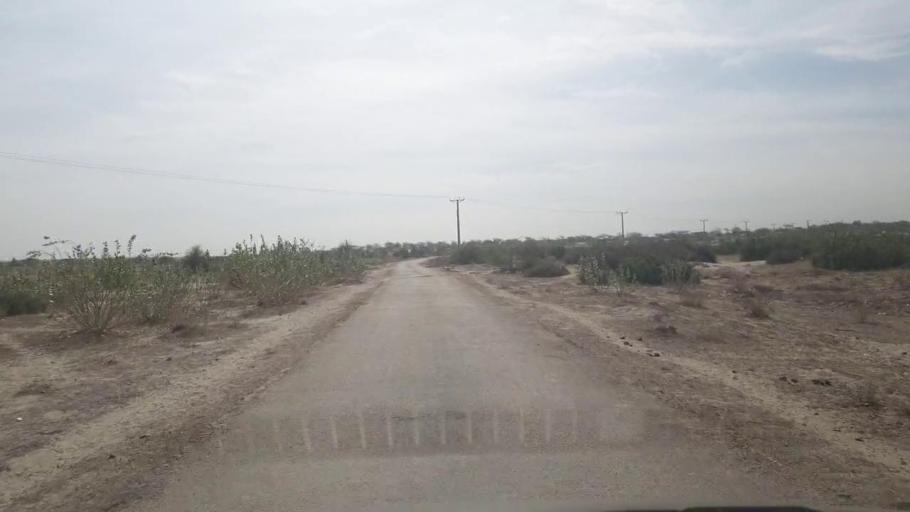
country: PK
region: Sindh
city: Umarkot
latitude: 25.2830
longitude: 69.7435
